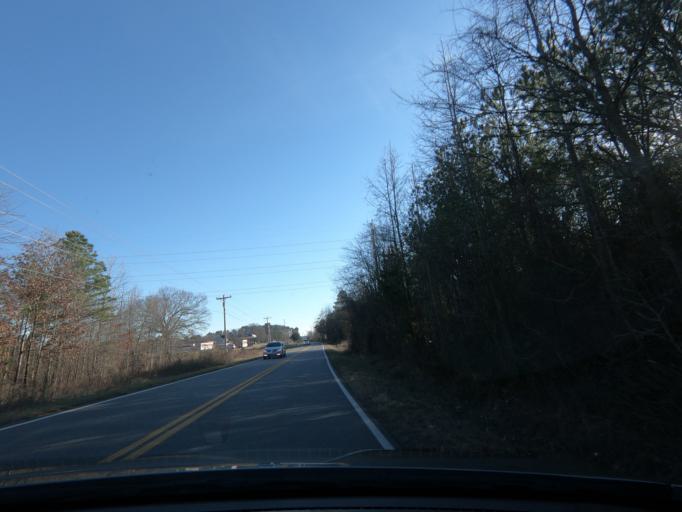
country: US
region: Georgia
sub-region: Gordon County
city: Calhoun
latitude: 34.4535
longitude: -84.9147
